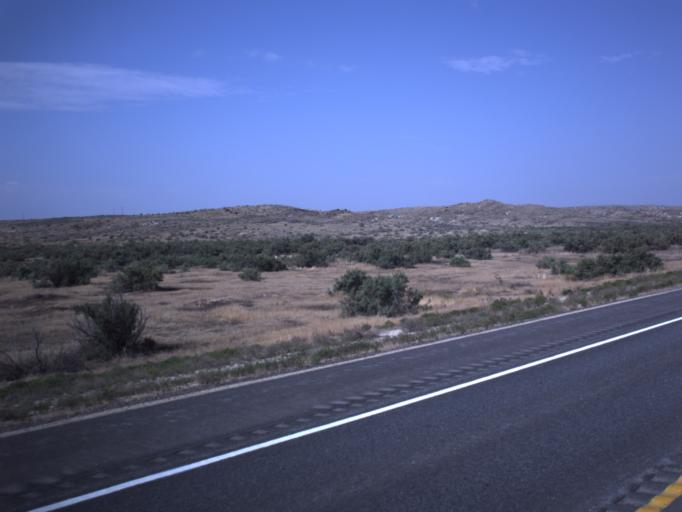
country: US
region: Utah
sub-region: Uintah County
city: Naples
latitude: 40.2872
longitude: -109.1406
